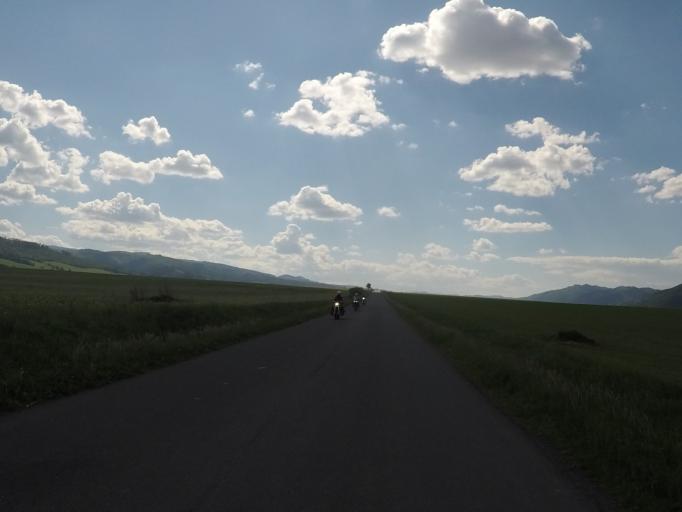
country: SK
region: Presovsky
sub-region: Okres Poprad
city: Poprad
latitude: 48.9942
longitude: 20.3484
